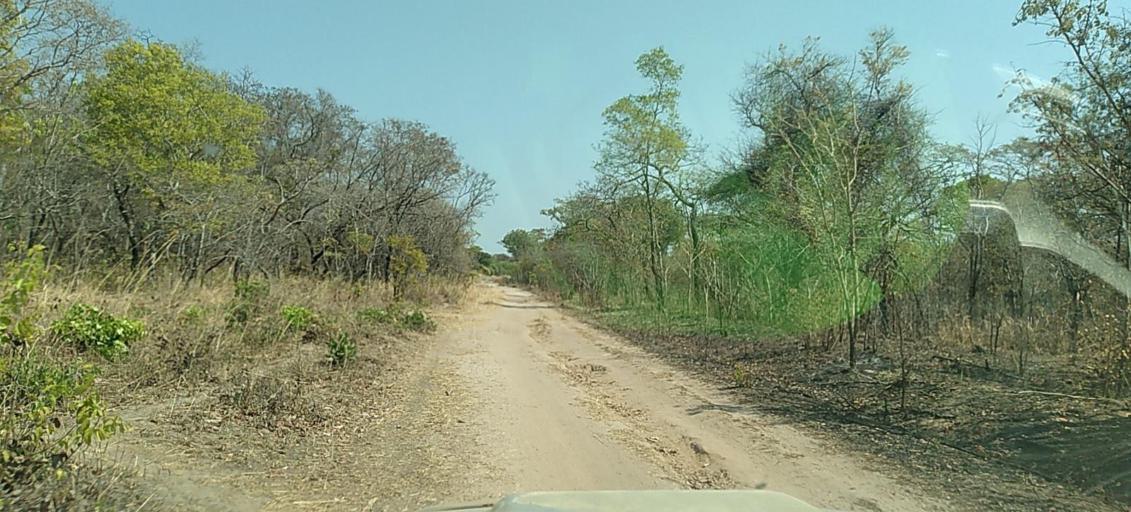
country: ZM
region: North-Western
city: Kalengwa
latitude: -13.2970
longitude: 24.7915
